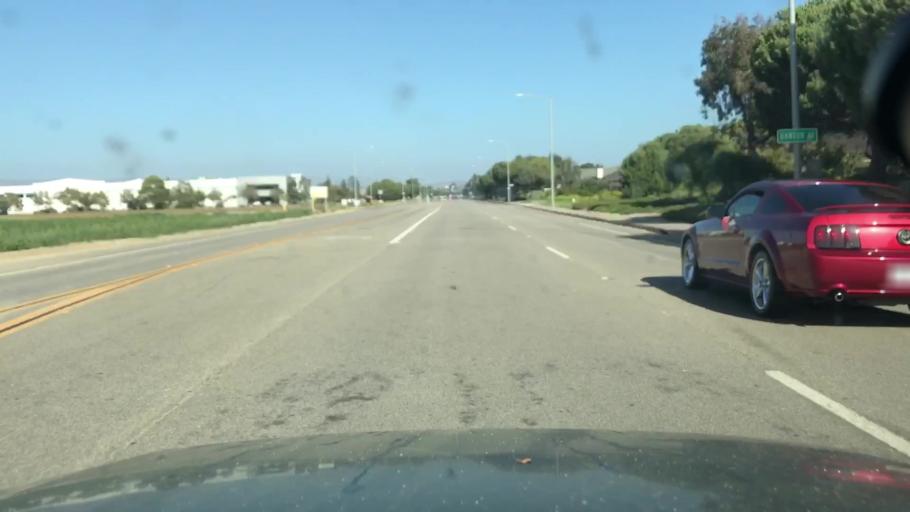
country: US
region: California
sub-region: Santa Barbara County
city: Lompoc
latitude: 34.6609
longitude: -120.4720
